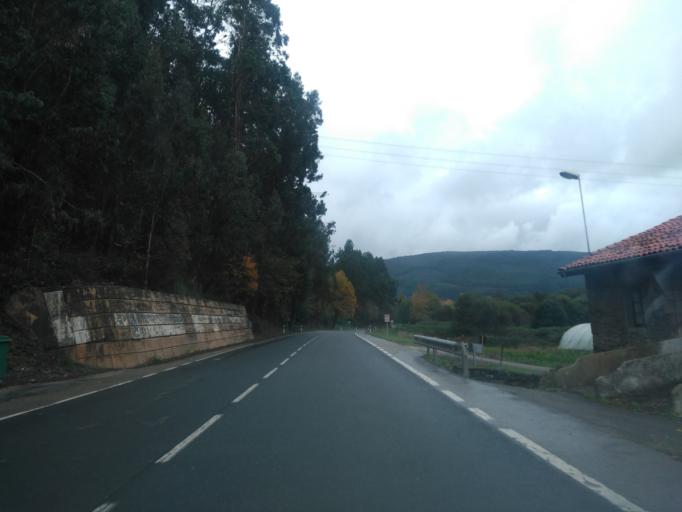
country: ES
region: Cantabria
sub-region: Provincia de Cantabria
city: Puente Viesgo
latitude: 43.3080
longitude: -3.9610
